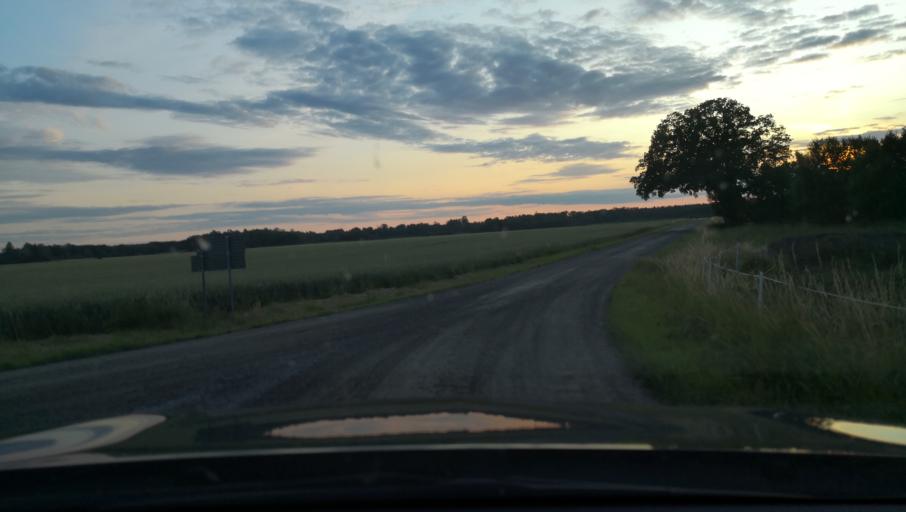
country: SE
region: Uppsala
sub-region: Osthammars Kommun
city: Bjorklinge
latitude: 60.0551
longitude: 17.5973
